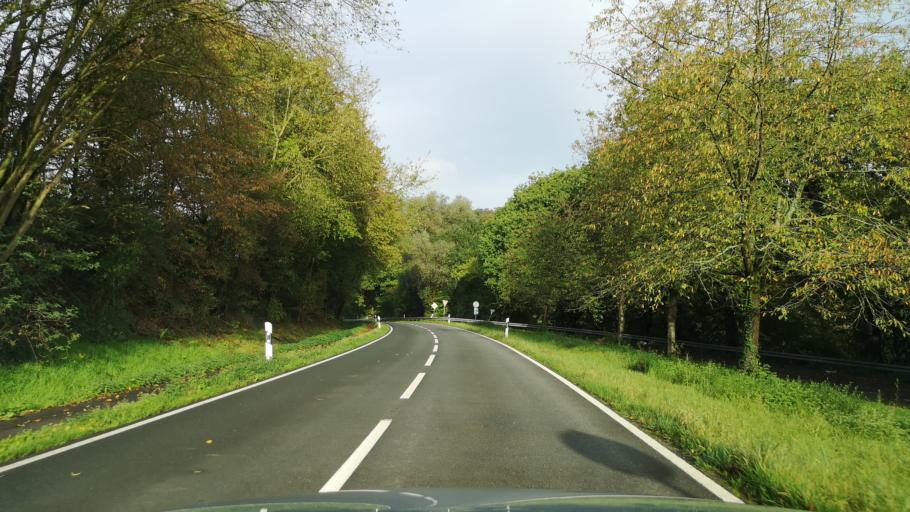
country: DE
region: North Rhine-Westphalia
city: Hattingen
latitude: 51.3594
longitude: 7.1608
